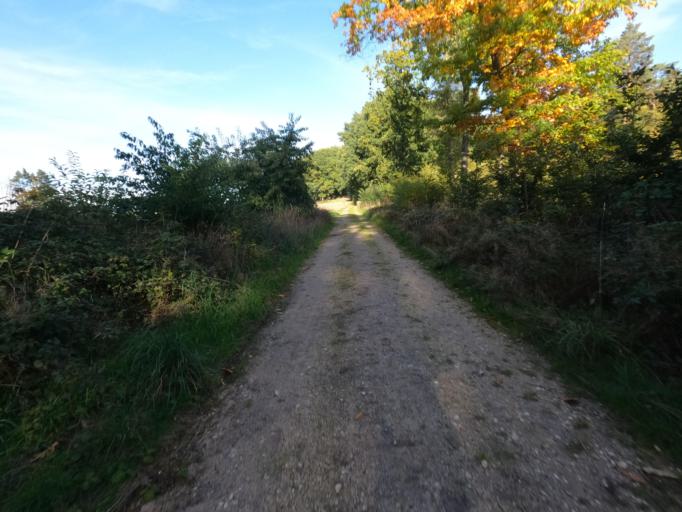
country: DE
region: North Rhine-Westphalia
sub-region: Regierungsbezirk Dusseldorf
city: Niederkruchten
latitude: 51.1751
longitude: 6.2223
